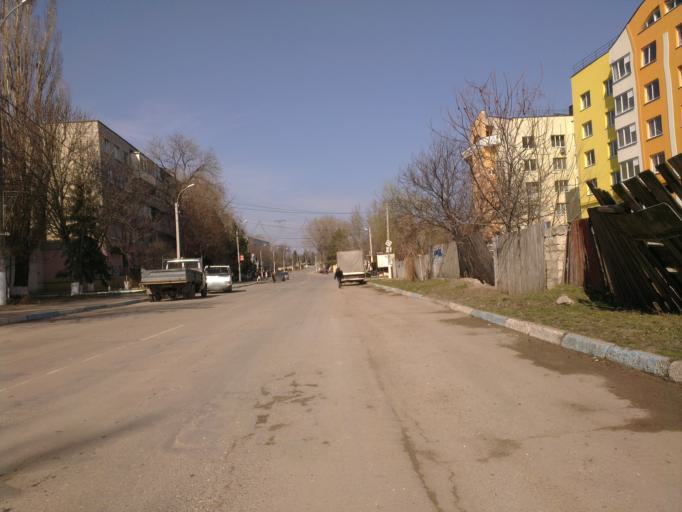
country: MD
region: Chisinau
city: Cricova
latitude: 47.1386
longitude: 28.8662
